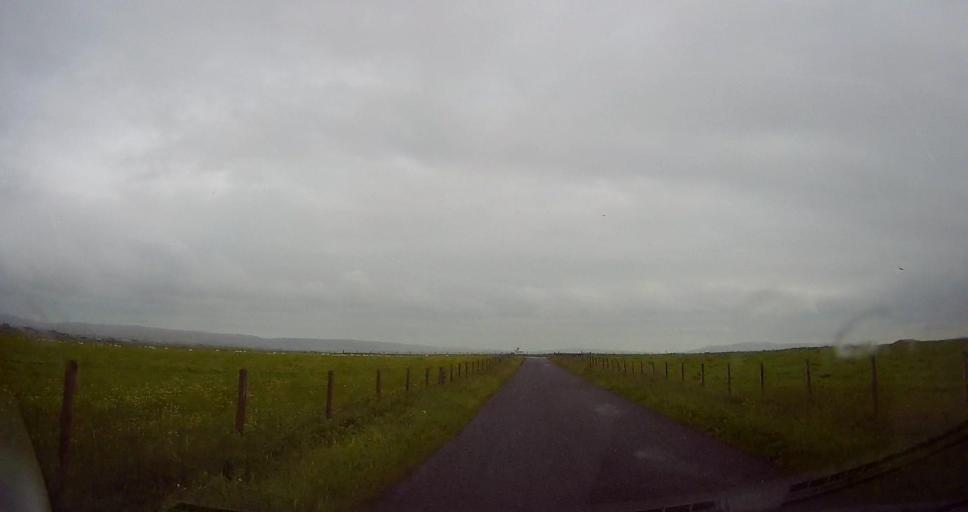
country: GB
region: Scotland
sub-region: Orkney Islands
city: Stromness
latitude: 59.0694
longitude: -3.2829
